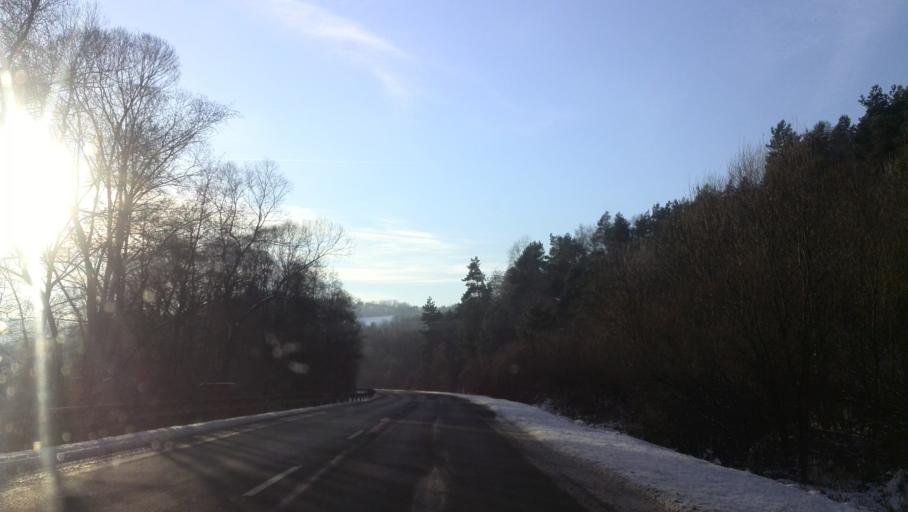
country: SK
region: Presovsky
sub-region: Okres Presov
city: Presov
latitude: 48.9618
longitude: 21.1213
